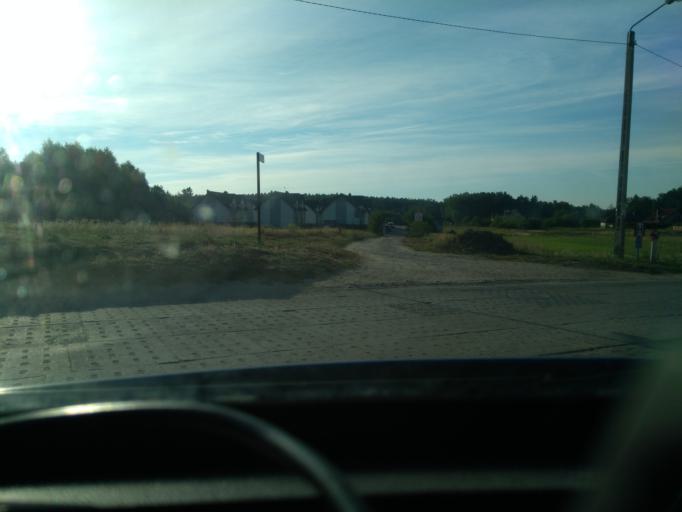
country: PL
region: Pomeranian Voivodeship
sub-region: Powiat kartuski
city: Banino
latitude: 54.4000
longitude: 18.3978
